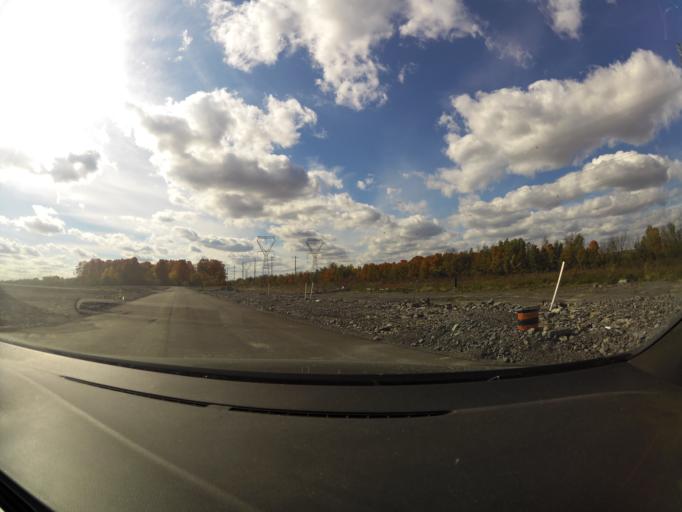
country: CA
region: Ontario
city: Bells Corners
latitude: 45.2718
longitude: -75.8960
